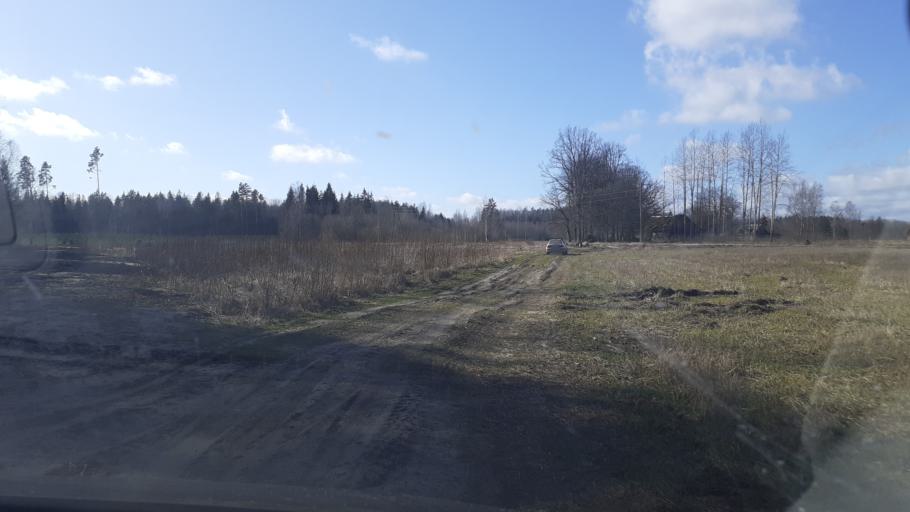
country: LV
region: Kuldigas Rajons
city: Kuldiga
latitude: 56.8760
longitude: 22.1089
